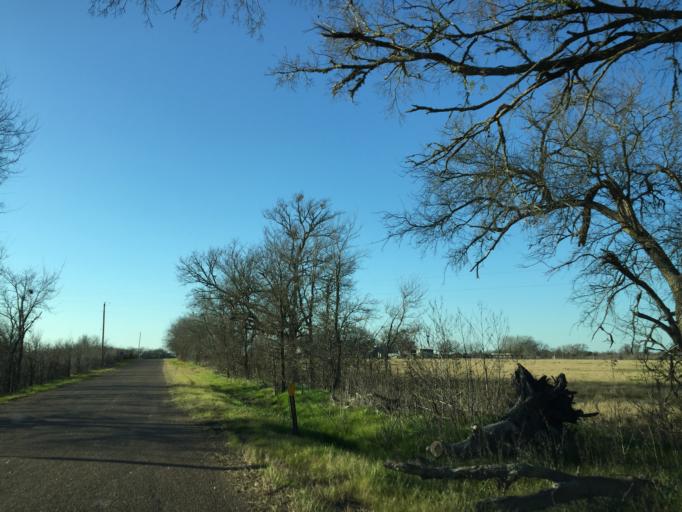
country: US
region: Texas
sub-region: Bastrop County
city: Elgin
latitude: 30.3731
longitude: -97.3119
